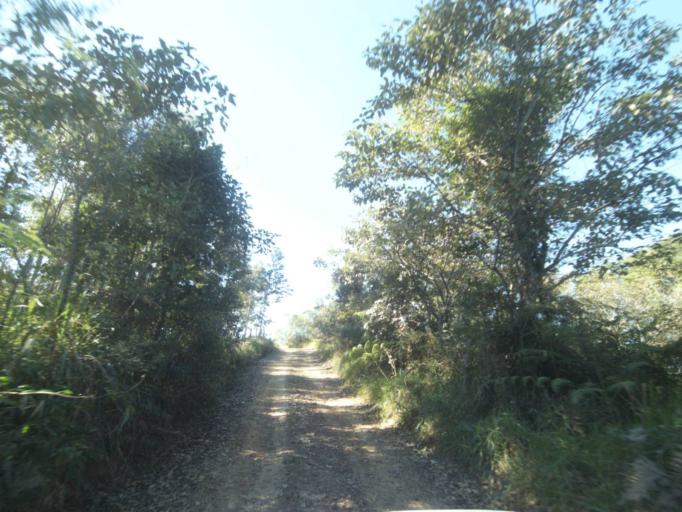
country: BR
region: Parana
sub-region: Tibagi
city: Tibagi
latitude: -24.5748
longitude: -50.4762
